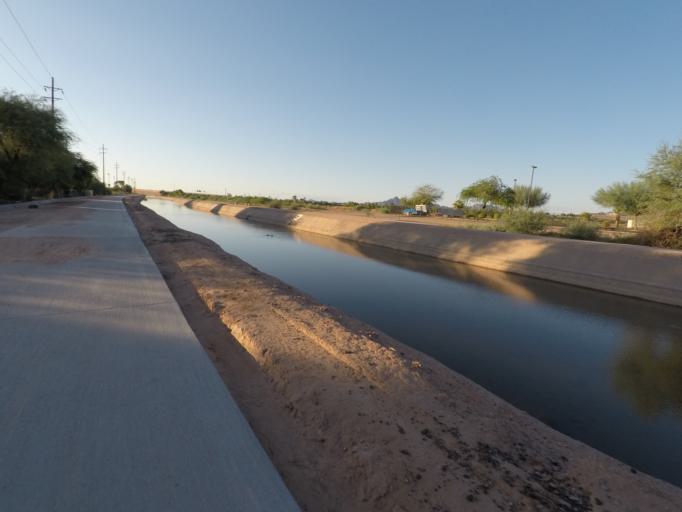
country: US
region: Arizona
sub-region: Maricopa County
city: Tempe Junction
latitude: 33.4537
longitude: -111.9995
